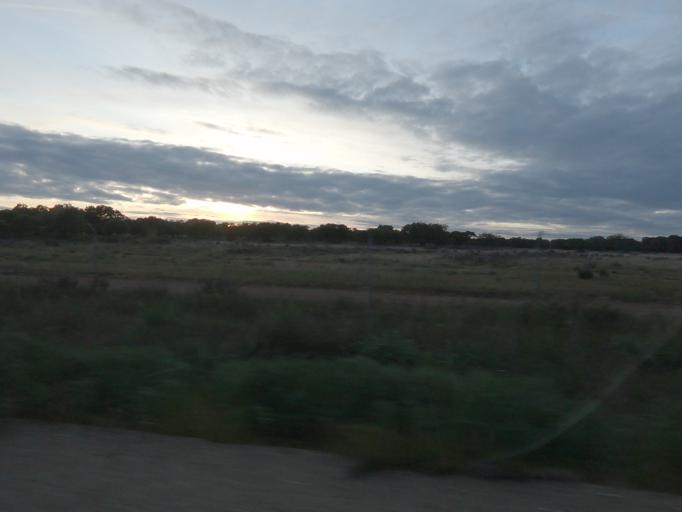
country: ES
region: Extremadura
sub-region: Provincia de Badajoz
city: Villar del Rey
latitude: 39.0102
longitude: -6.8567
